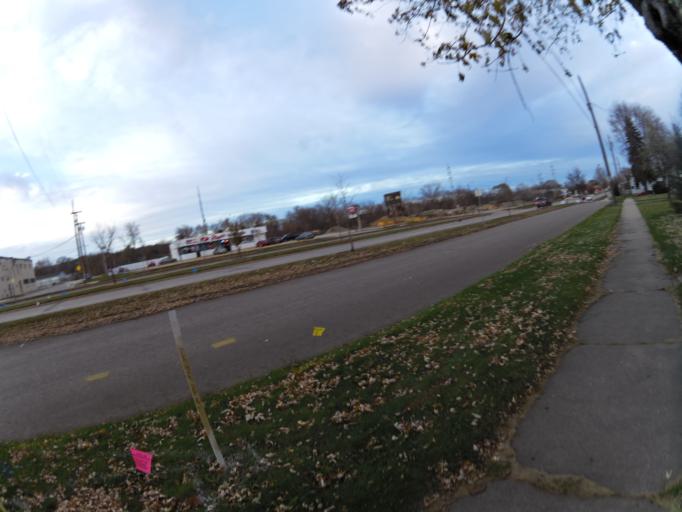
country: US
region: Minnesota
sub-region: Olmsted County
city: Rochester
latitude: 44.0279
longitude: -92.4752
